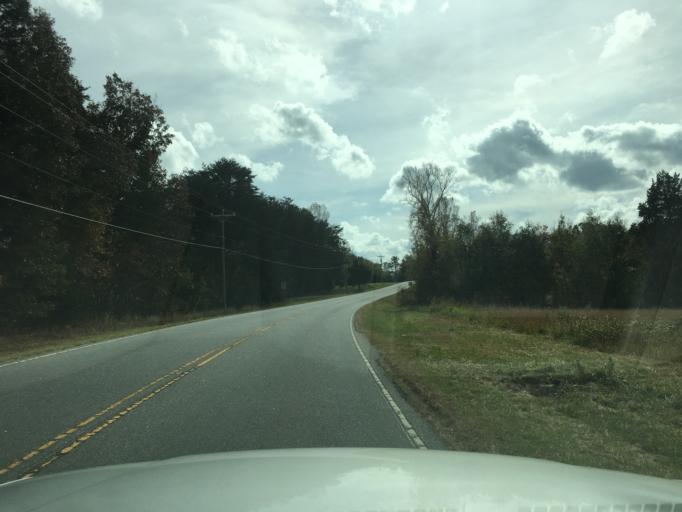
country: US
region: North Carolina
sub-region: Catawba County
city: Newton
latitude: 35.6650
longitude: -81.2721
